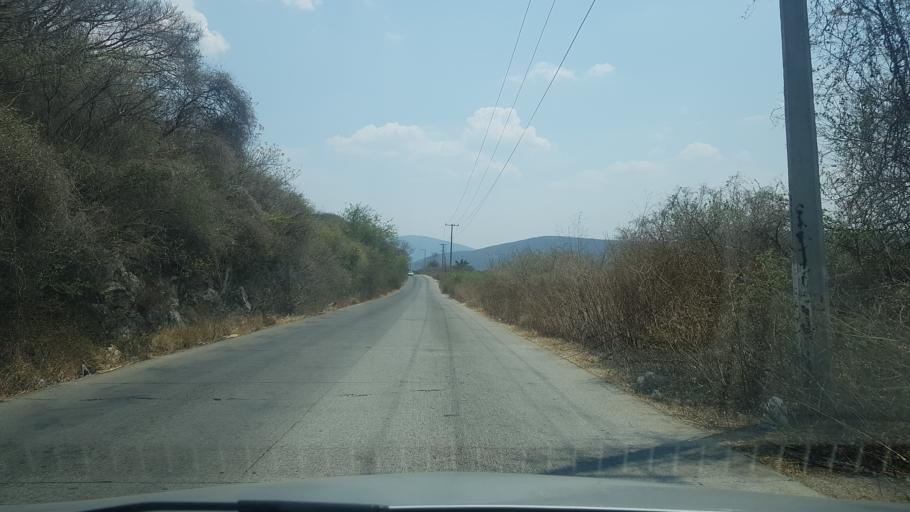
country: MX
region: Morelos
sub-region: Tlaltizapan de Zapata
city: Colonia Palo Prieto (Chipitongo)
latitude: 18.7416
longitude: -99.1140
